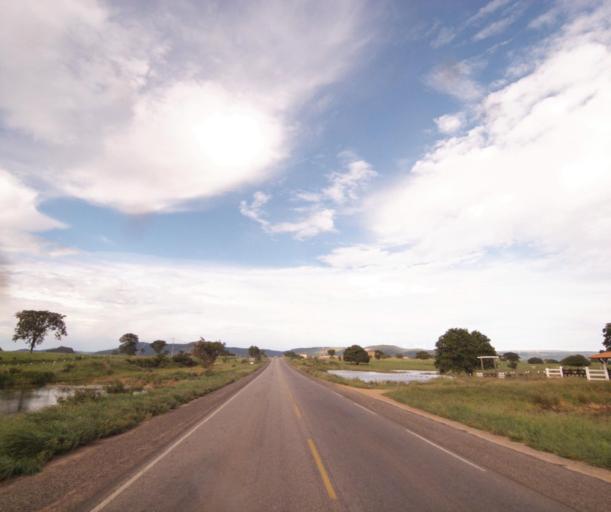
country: BR
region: Bahia
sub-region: Guanambi
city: Guanambi
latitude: -14.1954
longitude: -42.7490
